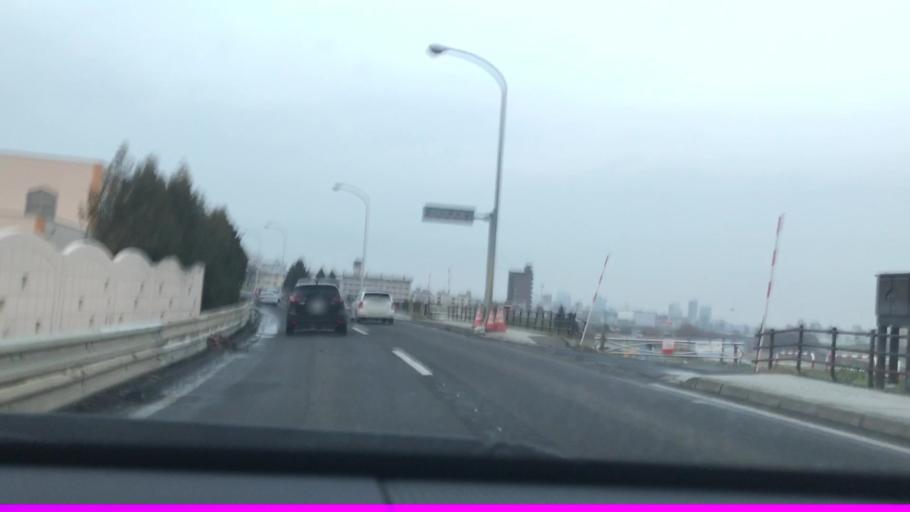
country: JP
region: Hokkaido
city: Sapporo
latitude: 43.0196
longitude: 141.3516
